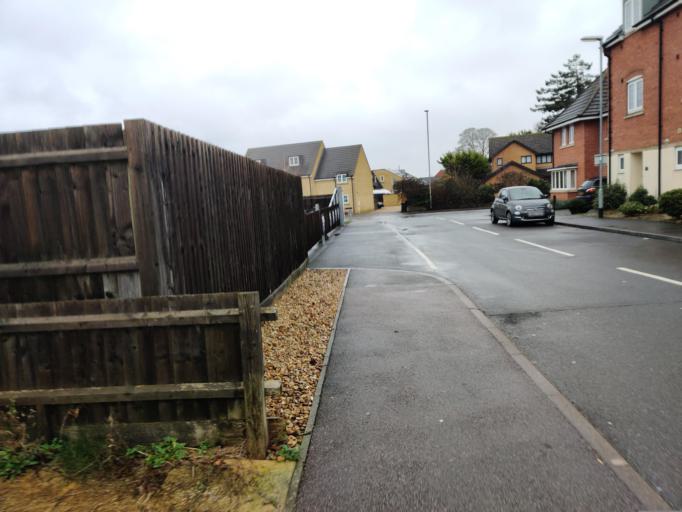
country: GB
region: England
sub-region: Lincolnshire
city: Bourne
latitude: 52.7646
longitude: -0.3752
